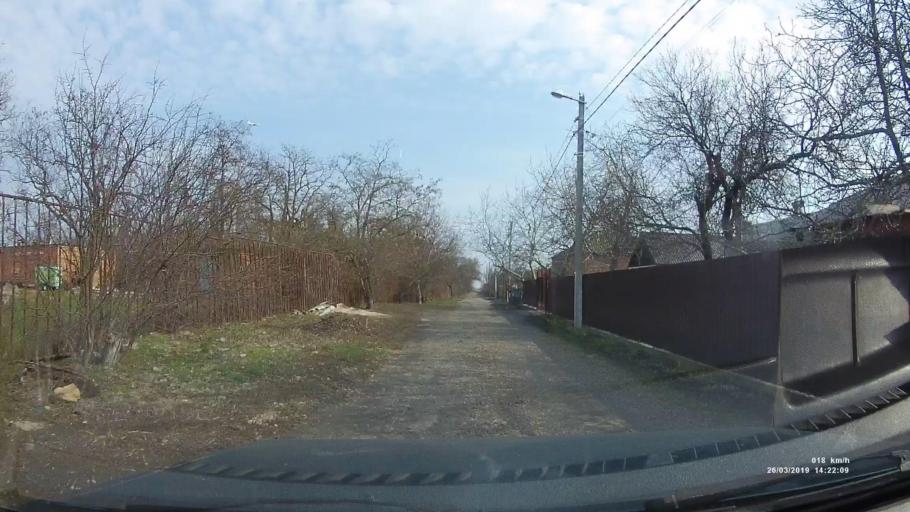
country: RU
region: Rostov
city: Novobessergenovka
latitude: 47.1848
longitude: 38.8680
